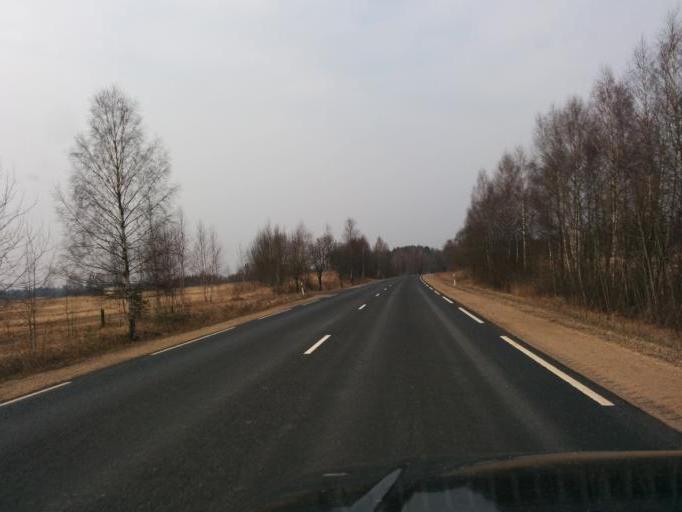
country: LV
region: Kekava
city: Kekava
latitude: 56.8162
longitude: 24.2855
